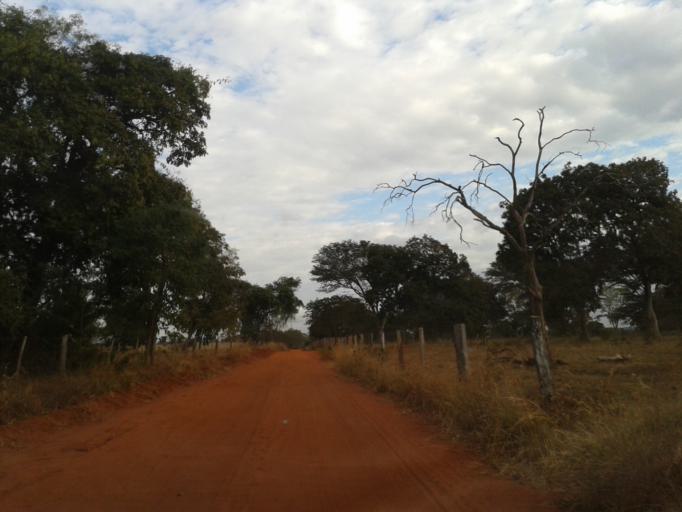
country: BR
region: Minas Gerais
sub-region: Santa Vitoria
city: Santa Vitoria
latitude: -18.7655
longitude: -50.1877
